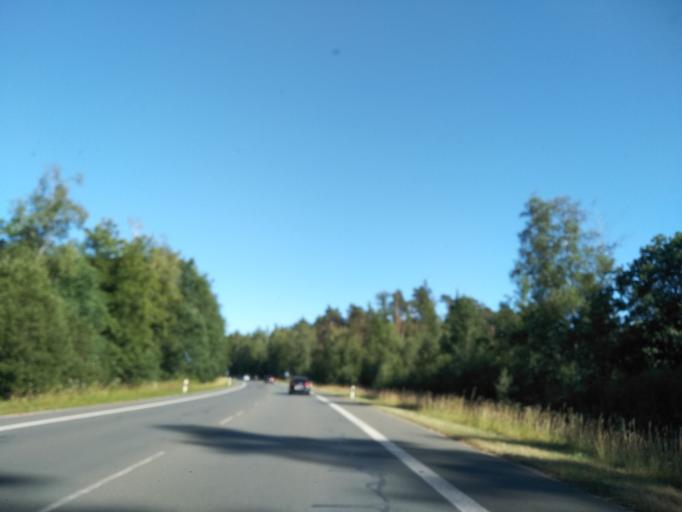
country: DE
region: Bavaria
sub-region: Regierungsbezirk Mittelfranken
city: Hessdorf
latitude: 49.6188
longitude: 10.9528
